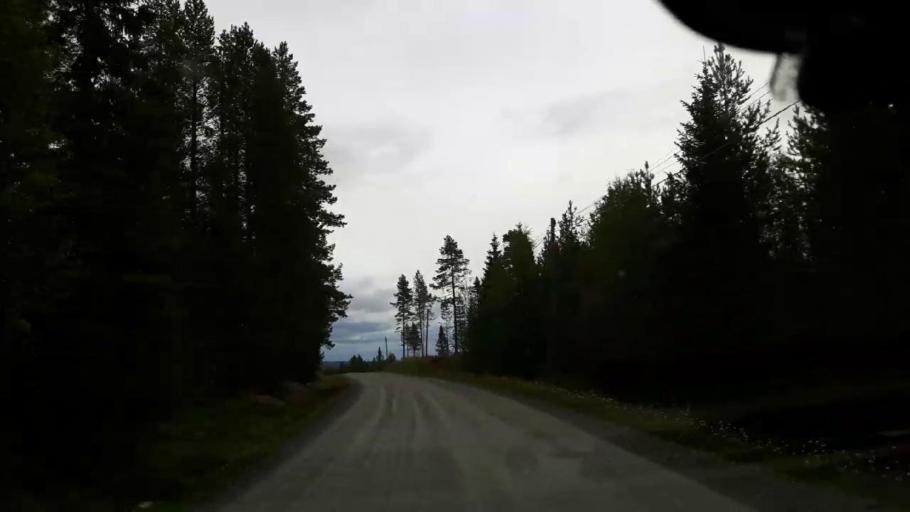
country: SE
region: Jaemtland
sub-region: Krokoms Kommun
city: Valla
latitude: 63.6887
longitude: 13.8701
